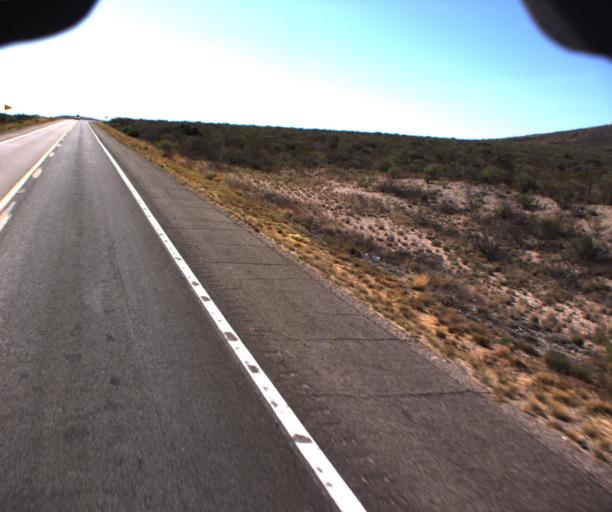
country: US
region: Arizona
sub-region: Cochise County
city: Tombstone
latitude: 31.6912
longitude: -110.0384
